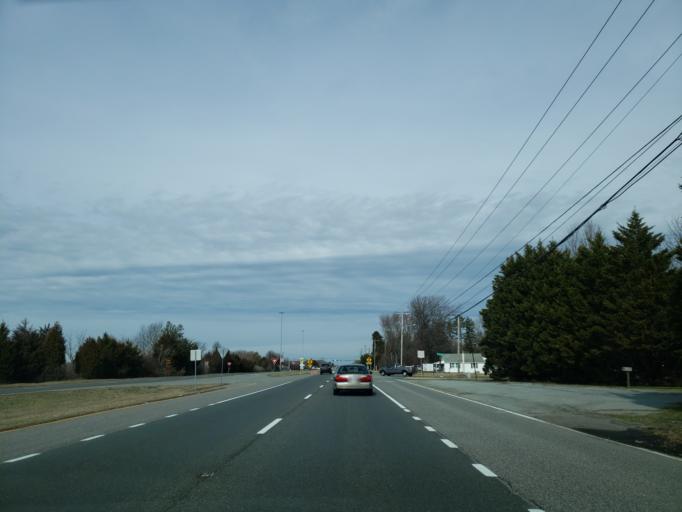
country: US
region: Delaware
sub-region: Kent County
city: Smyrna
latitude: 39.3328
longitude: -75.6268
